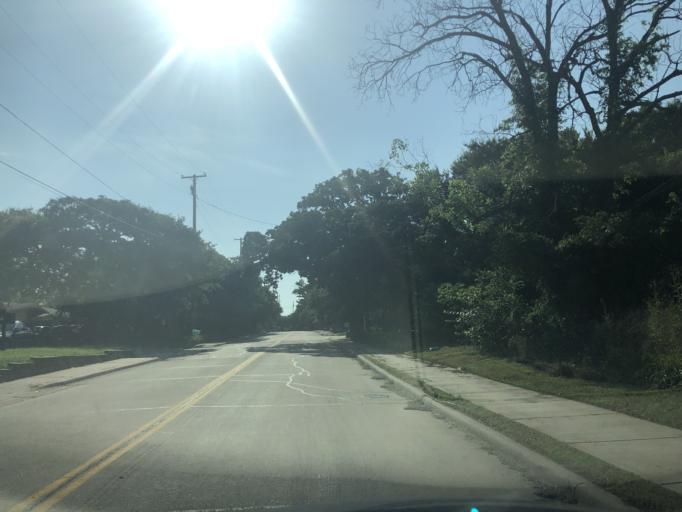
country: US
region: Texas
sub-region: Dallas County
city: Irving
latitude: 32.8070
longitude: -96.9927
